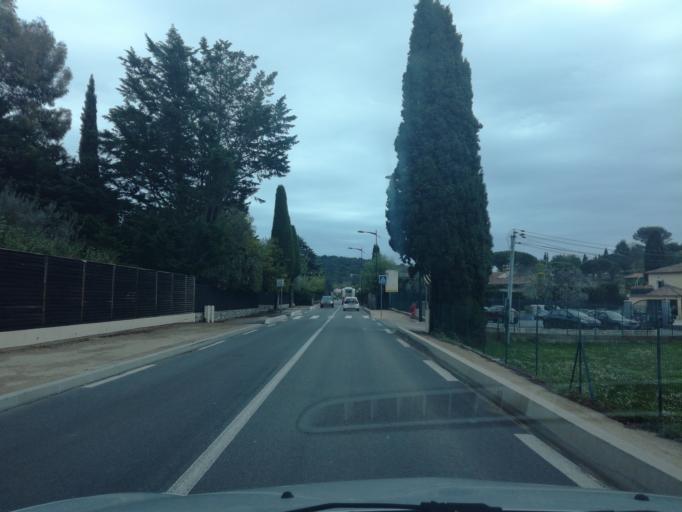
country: FR
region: Provence-Alpes-Cote d'Azur
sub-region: Departement des Alpes-Maritimes
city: Mougins
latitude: 43.6034
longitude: 7.0115
